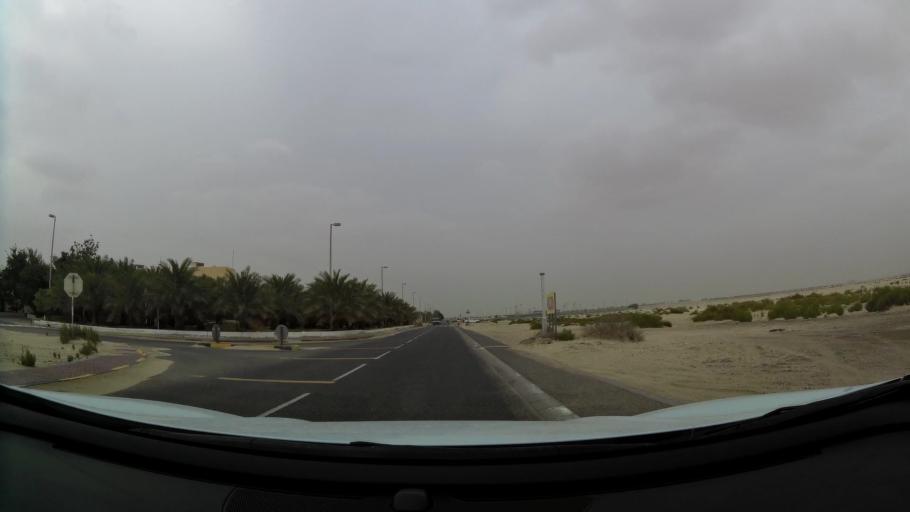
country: AE
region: Abu Dhabi
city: Abu Dhabi
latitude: 24.3766
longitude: 54.6729
